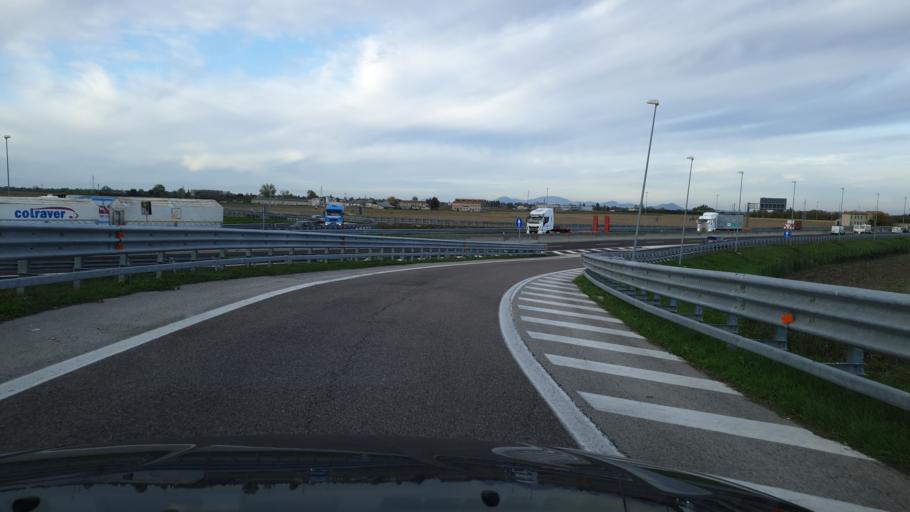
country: IT
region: Veneto
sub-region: Provincia di Rovigo
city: Villamarzana
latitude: 45.0234
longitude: 11.6958
